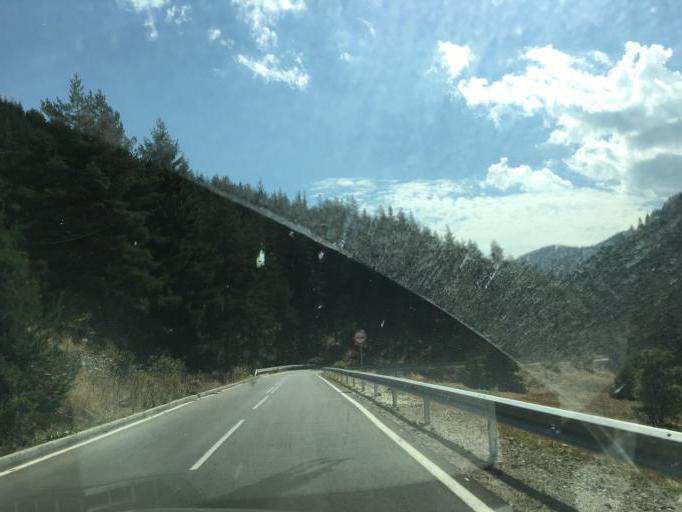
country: BG
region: Pazardzhik
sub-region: Obshtina Batak
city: Batak
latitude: 41.8901
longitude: 24.3319
